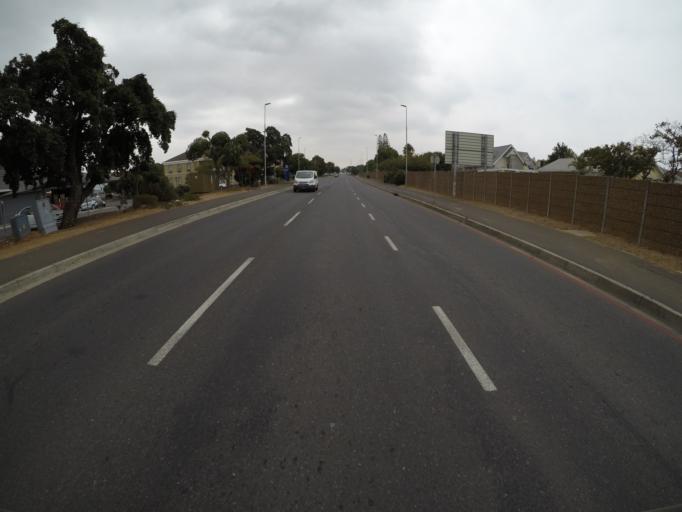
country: ZA
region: Western Cape
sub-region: City of Cape Town
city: Kraaifontein
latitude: -33.8760
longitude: 18.6376
